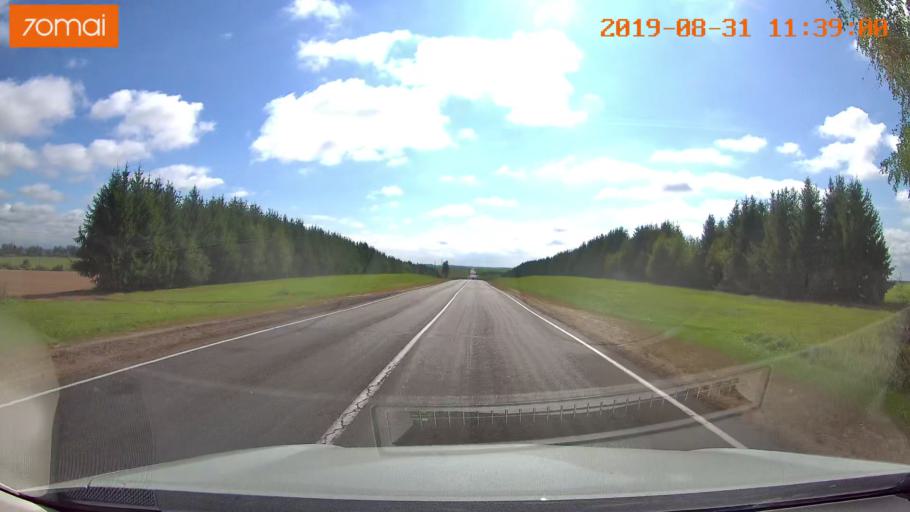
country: BY
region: Mogilev
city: Cherykaw
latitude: 53.6337
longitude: 31.2830
